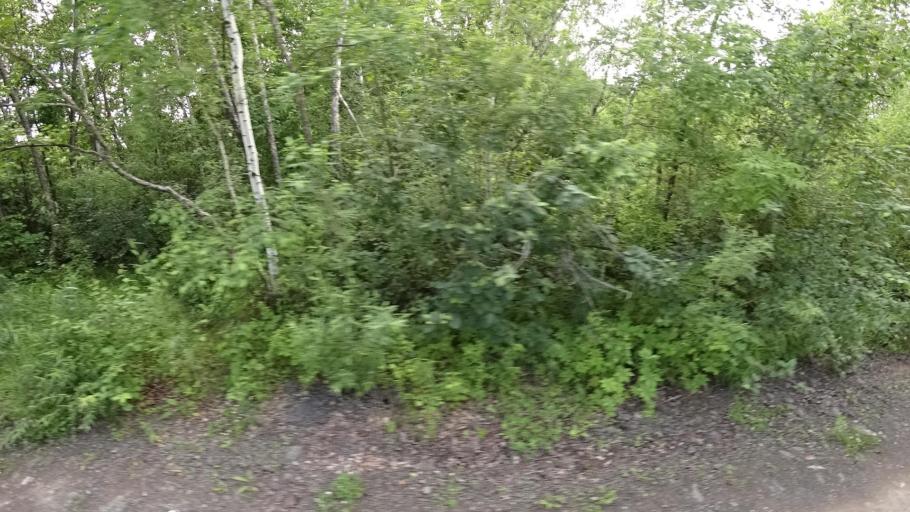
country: RU
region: Khabarovsk Krai
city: Litovko
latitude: 49.3606
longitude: 135.1806
